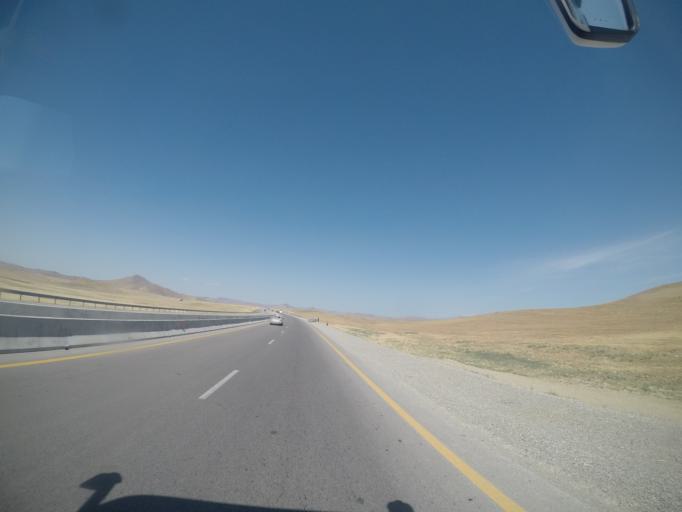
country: AZ
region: Sumqayit
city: Haci Zeynalabdin
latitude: 40.4856
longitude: 49.4263
